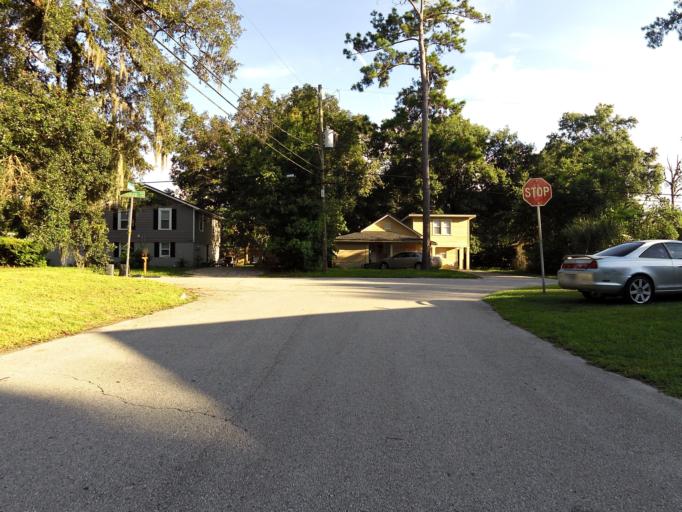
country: US
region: Florida
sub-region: Duval County
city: Jacksonville
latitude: 30.2986
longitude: -81.6296
